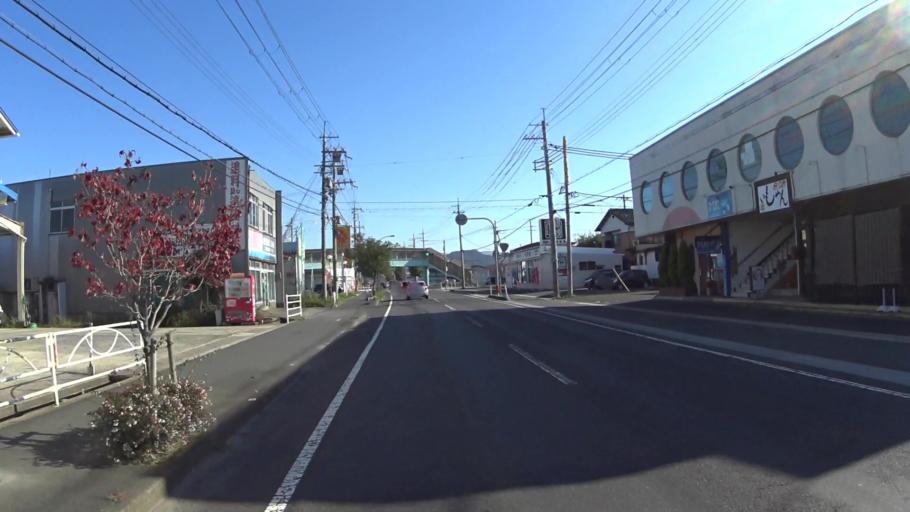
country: JP
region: Kyoto
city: Miyazu
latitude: 35.5932
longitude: 135.0922
